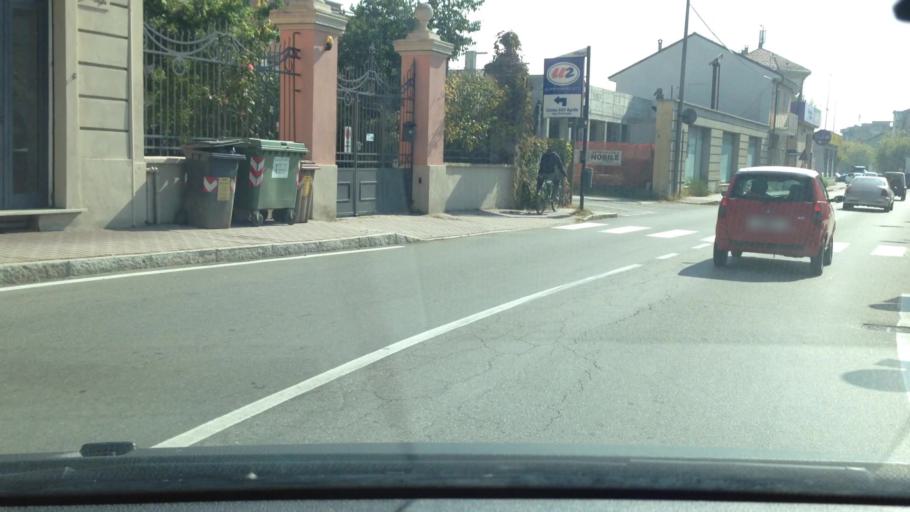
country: IT
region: Piedmont
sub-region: Provincia di Asti
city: Asti
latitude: 44.9070
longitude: 8.1847
